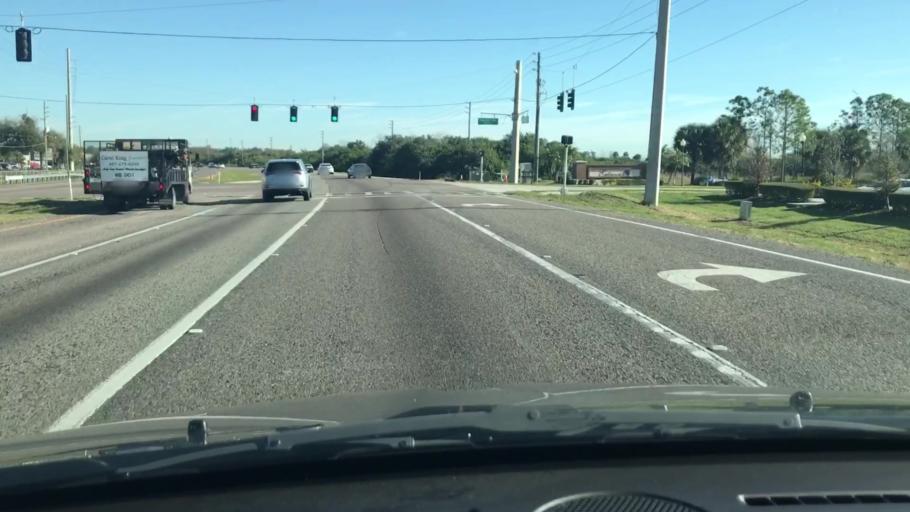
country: US
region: Florida
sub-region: Osceola County
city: Kissimmee
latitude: 28.2773
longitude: -81.4178
